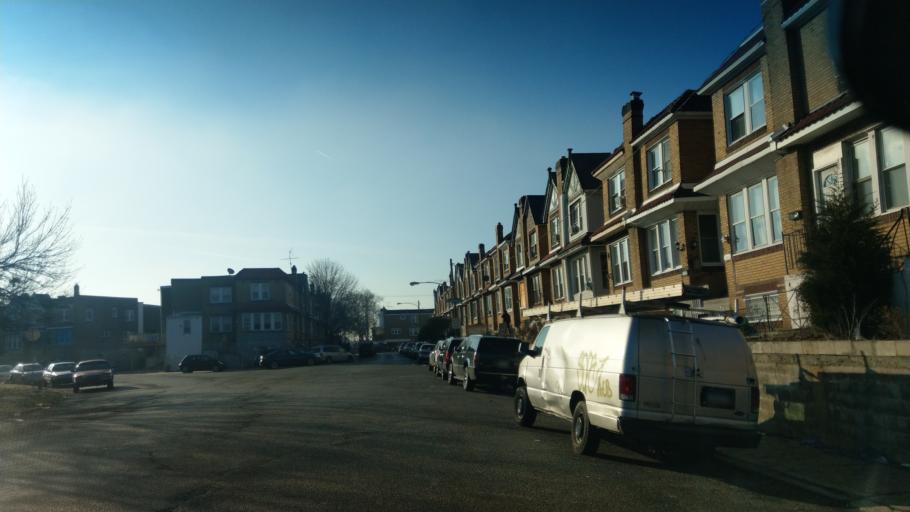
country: US
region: Pennsylvania
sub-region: Montgomery County
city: Rockledge
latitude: 40.0262
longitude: -75.1144
